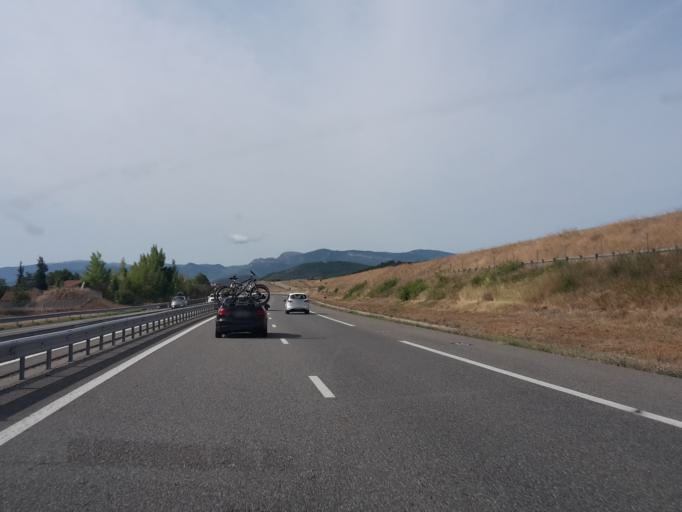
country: FR
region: Provence-Alpes-Cote d'Azur
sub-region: Departement des Hautes-Alpes
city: Laragne-Monteglin
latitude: 44.3723
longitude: 5.9269
